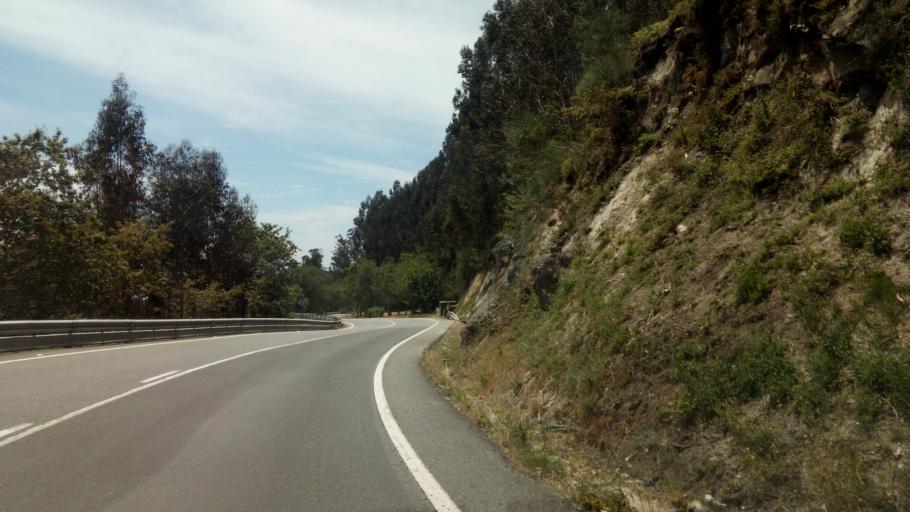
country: ES
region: Galicia
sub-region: Provincia de Pontevedra
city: Moana
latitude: 42.3161
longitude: -8.7257
